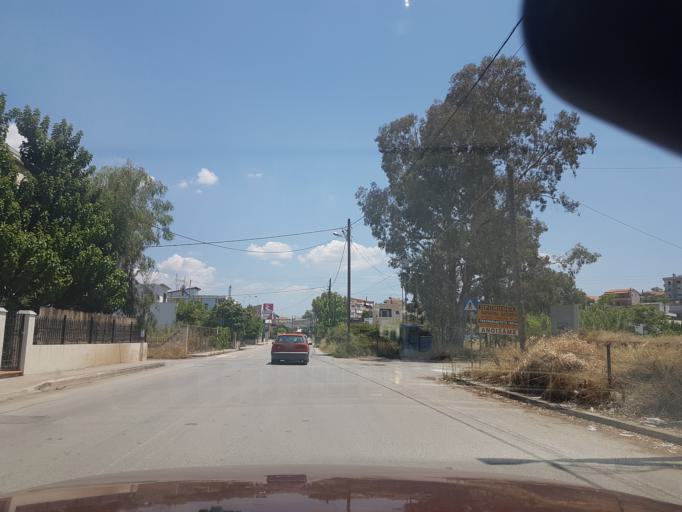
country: GR
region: Central Greece
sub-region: Nomos Evvoias
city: Chalkida
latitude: 38.4692
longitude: 23.6197
